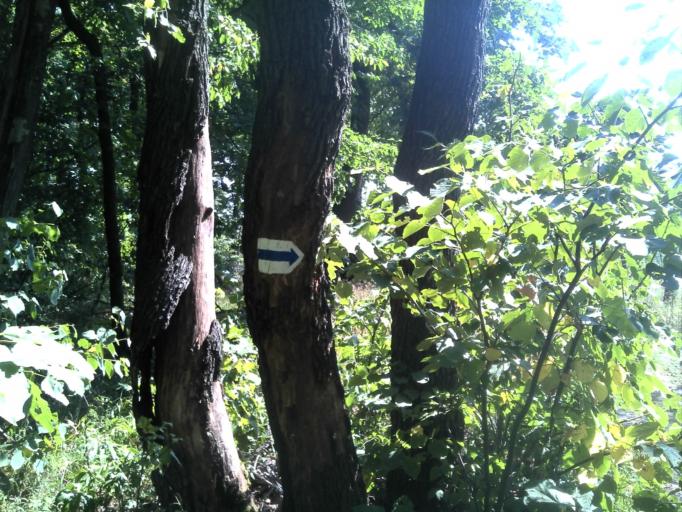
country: HU
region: Baranya
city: Pecs
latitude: 46.1291
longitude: 18.2074
